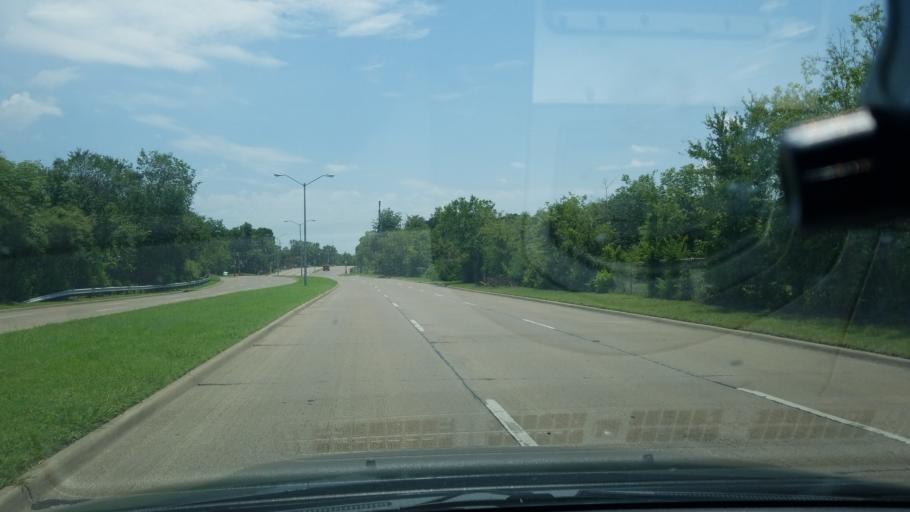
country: US
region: Texas
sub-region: Dallas County
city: Balch Springs
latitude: 32.7215
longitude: -96.6658
